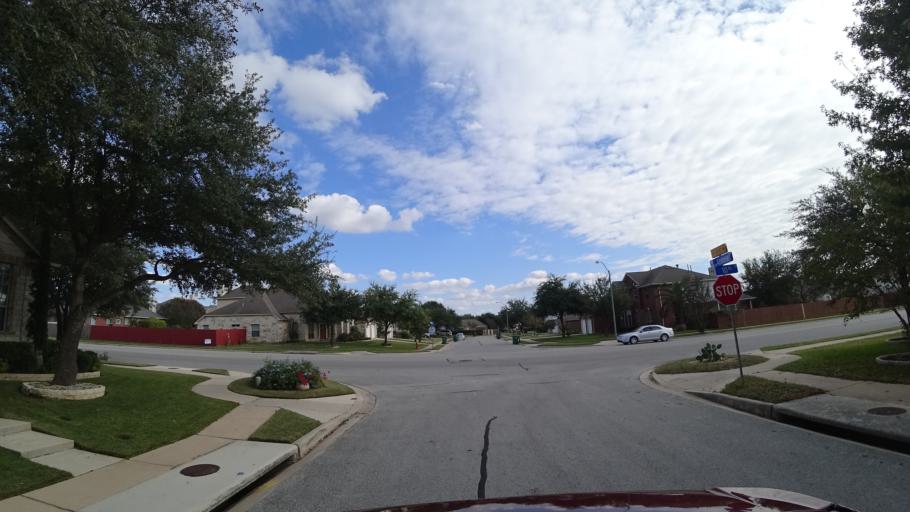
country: US
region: Texas
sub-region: Travis County
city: Pflugerville
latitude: 30.4324
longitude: -97.6334
